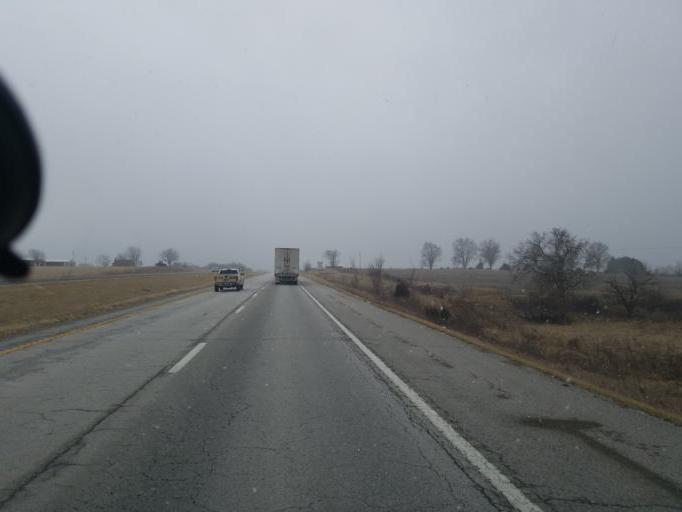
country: US
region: Missouri
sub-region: Macon County
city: La Plata
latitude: 39.9177
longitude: -92.4745
